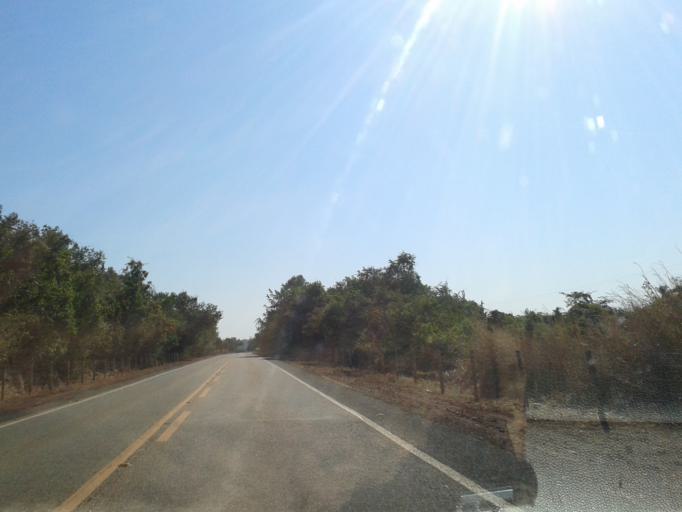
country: BR
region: Goias
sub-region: Mozarlandia
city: Mozarlandia
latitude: -14.6684
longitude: -50.5333
